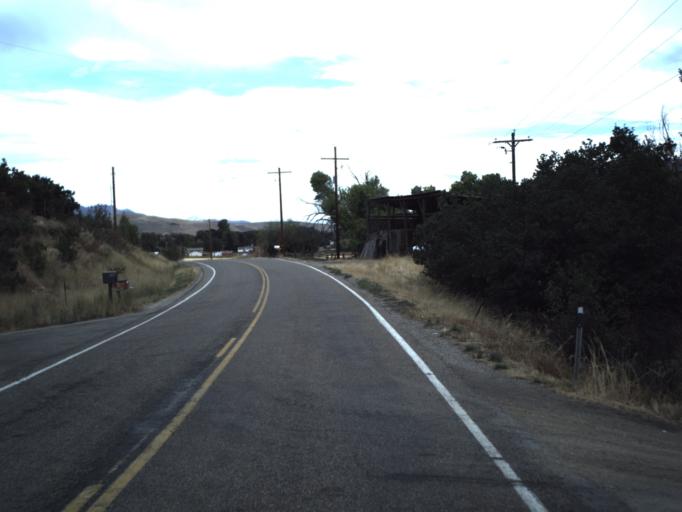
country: US
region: Utah
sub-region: Morgan County
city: Morgan
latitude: 40.9607
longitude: -111.6681
